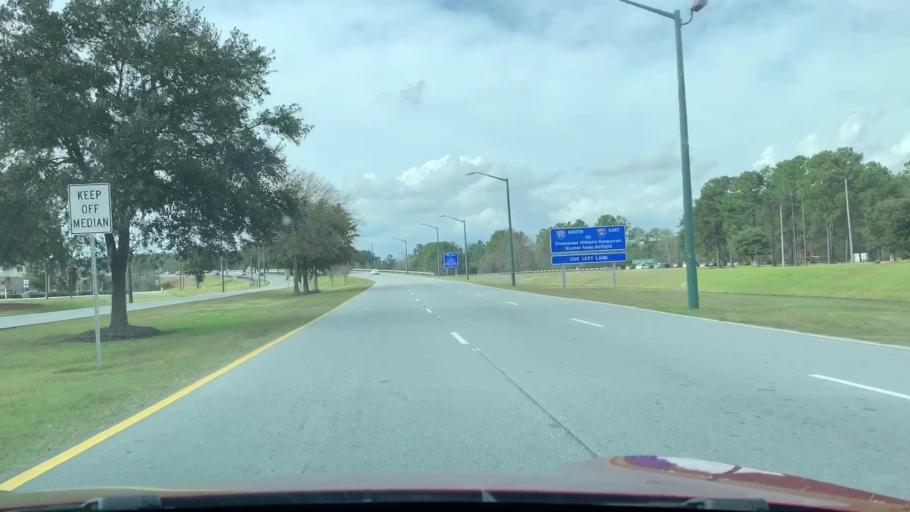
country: US
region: Georgia
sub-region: Chatham County
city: Pooler
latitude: 32.1400
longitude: -81.2350
